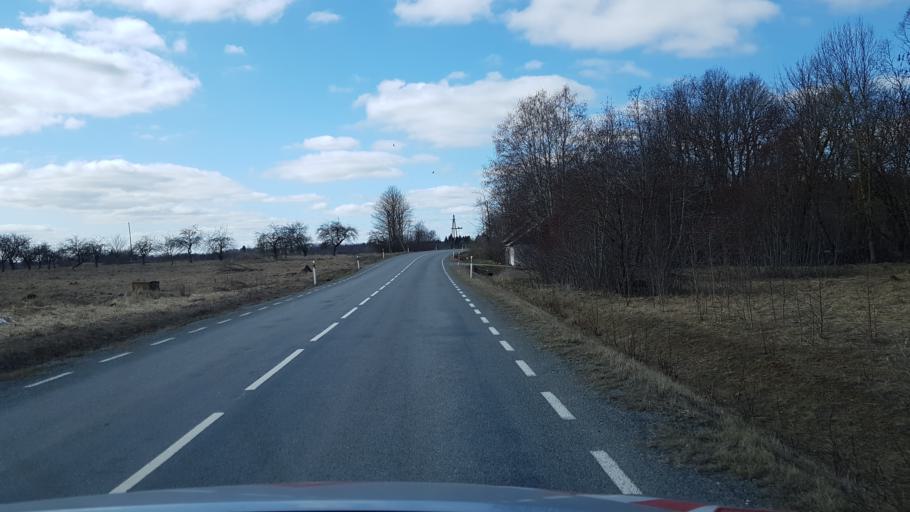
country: EE
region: Laeaene-Virumaa
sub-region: Tapa vald
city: Tapa
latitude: 59.2689
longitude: 25.9334
